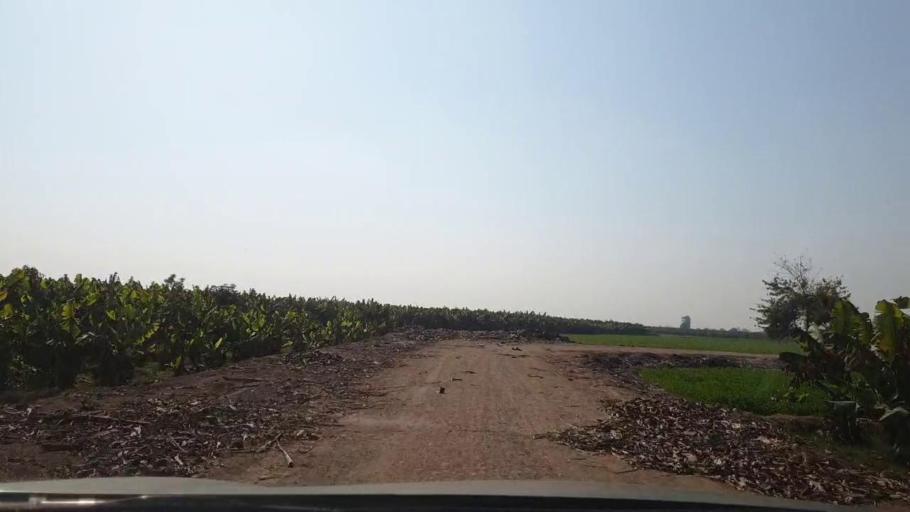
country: PK
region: Sindh
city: Tando Allahyar
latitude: 25.5012
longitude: 68.6898
